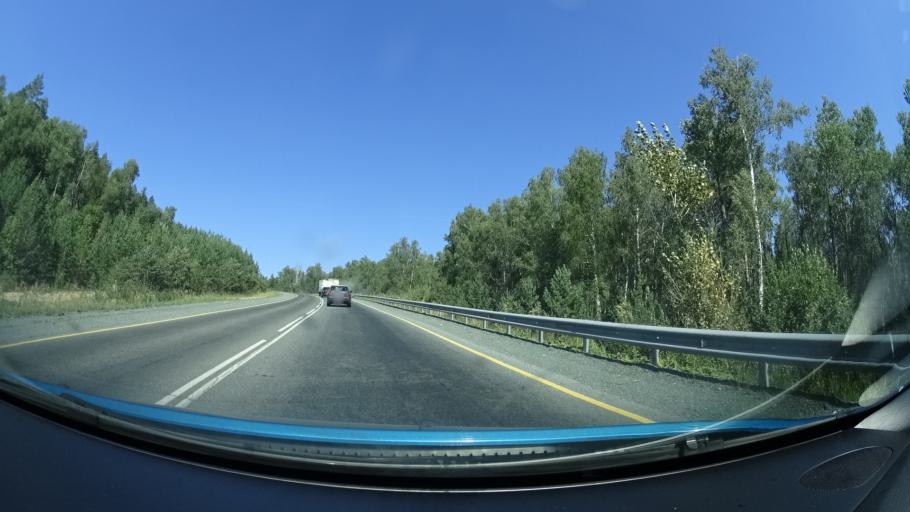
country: RU
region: Bashkortostan
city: Abzakovo
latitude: 53.8887
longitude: 58.5246
